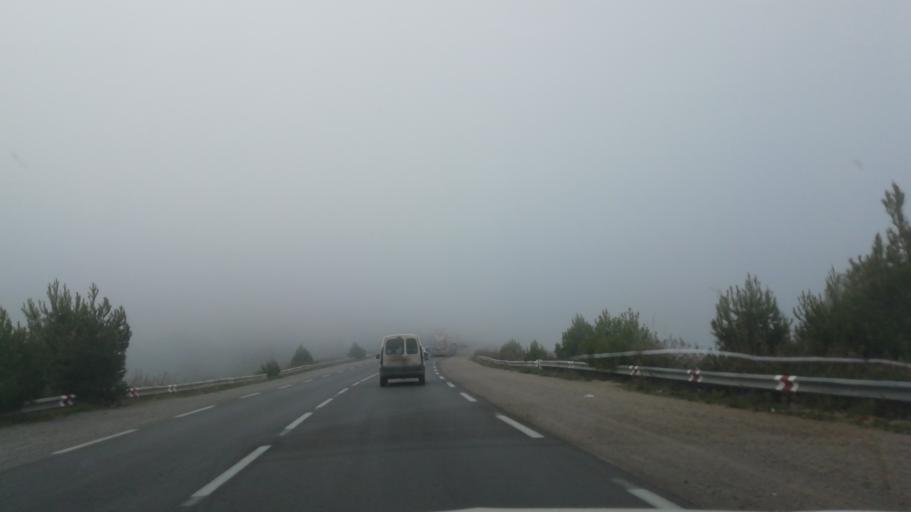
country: DZ
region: Mascara
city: Mascara
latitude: 35.5274
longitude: 0.3299
